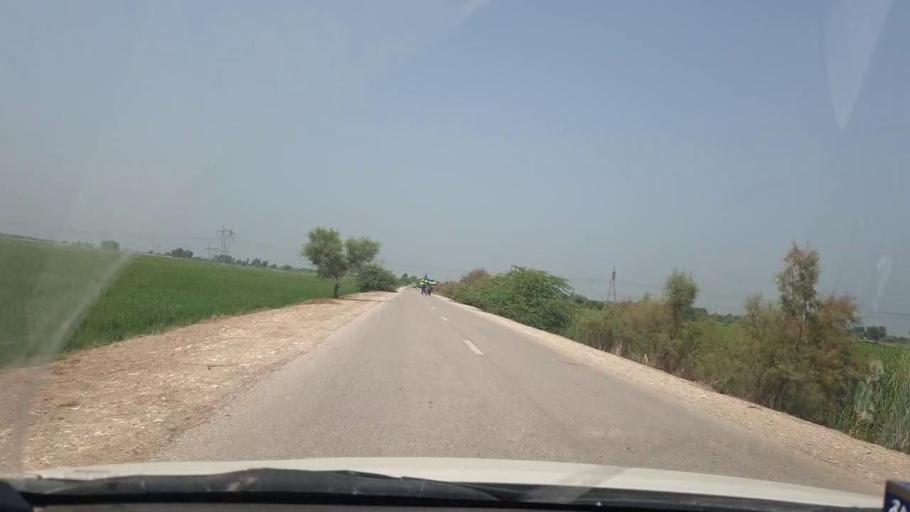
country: PK
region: Sindh
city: Rustam jo Goth
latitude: 27.9567
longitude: 68.7393
